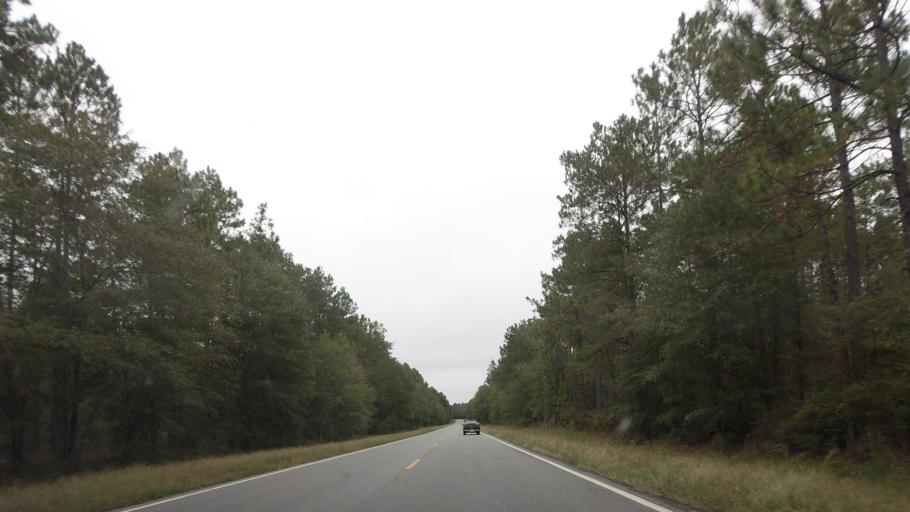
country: US
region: Georgia
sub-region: Berrien County
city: Enigma
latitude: 31.4129
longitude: -83.2427
